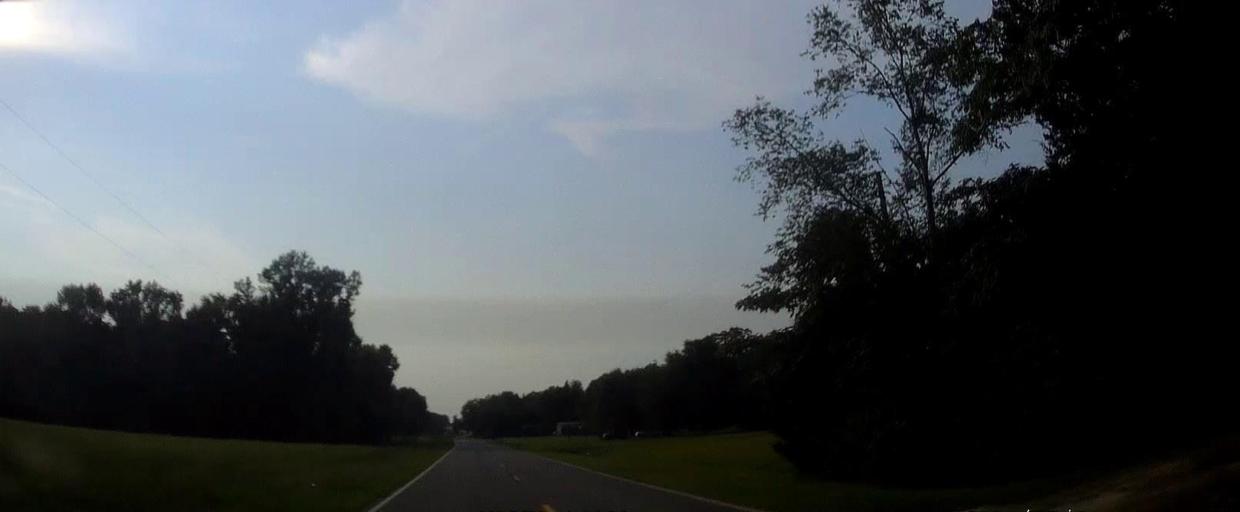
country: US
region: Georgia
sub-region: Laurens County
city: Dublin
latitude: 32.4875
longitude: -82.9767
